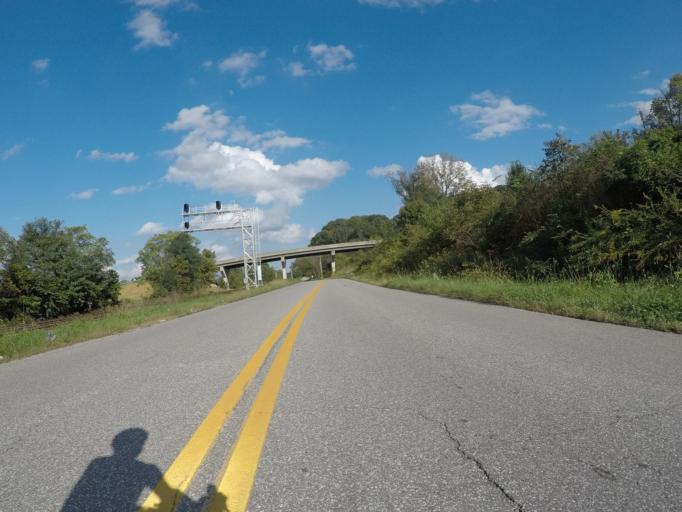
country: US
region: Ohio
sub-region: Lawrence County
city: Burlington
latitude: 38.3963
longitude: -82.5179
